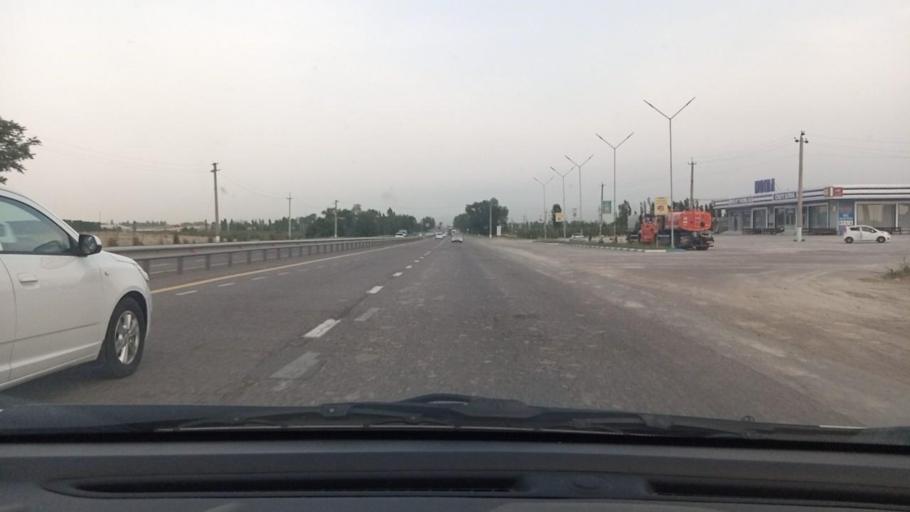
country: UZ
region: Toshkent
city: Ohangaron
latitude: 40.9398
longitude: 69.5833
